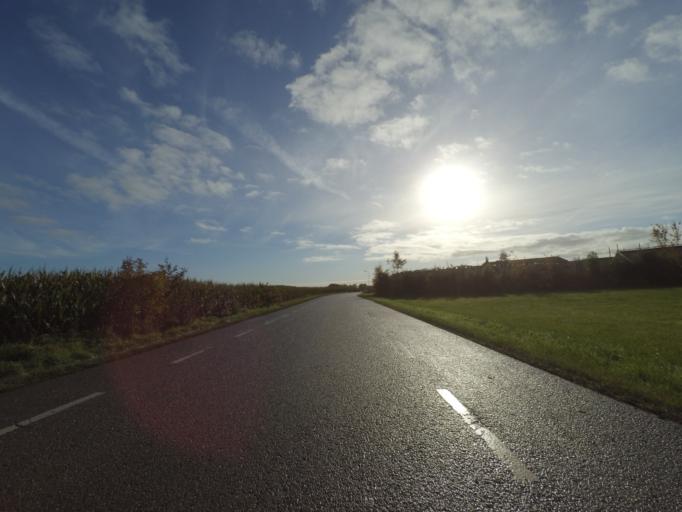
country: NL
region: Utrecht
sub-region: Gemeente Utrechtse Heuvelrug
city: Driebergen-Rijsenburg
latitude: 52.0131
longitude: 5.2602
